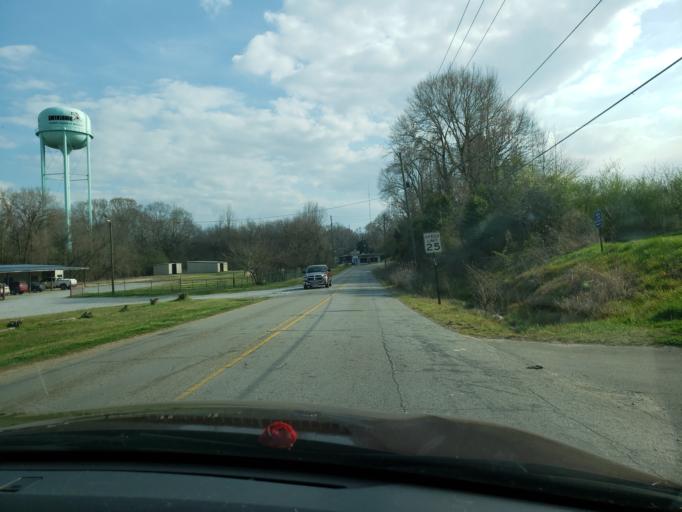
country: US
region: Alabama
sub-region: Hale County
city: Greensboro
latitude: 32.7014
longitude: -87.6069
